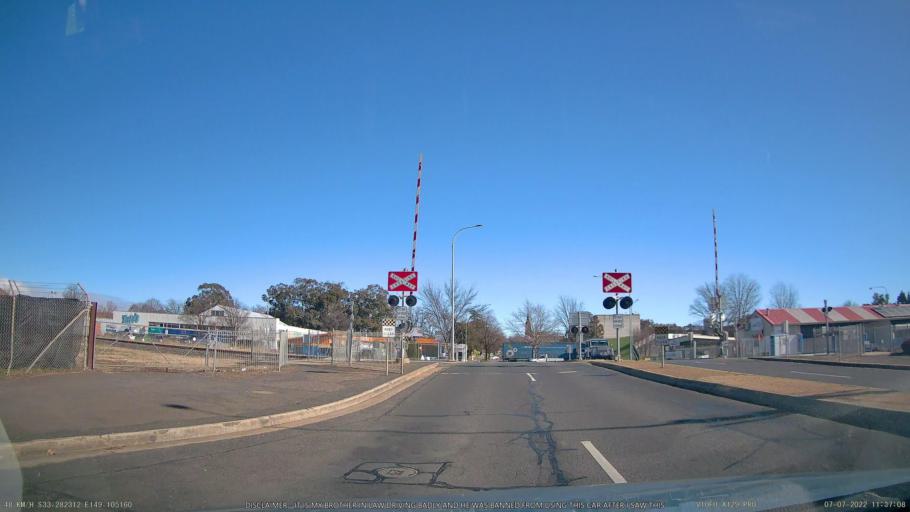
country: AU
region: New South Wales
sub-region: Orange Municipality
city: Orange
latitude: -33.2821
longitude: 149.1051
